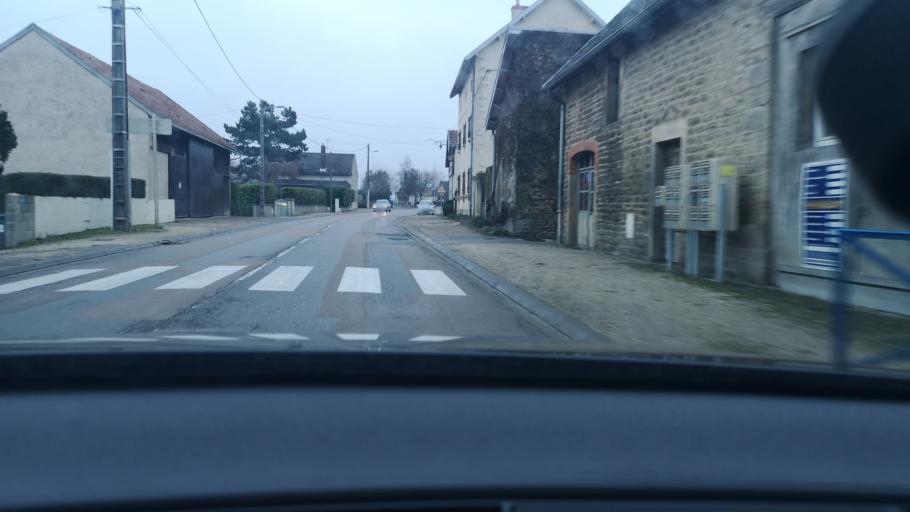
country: FR
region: Bourgogne
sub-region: Departement de la Cote-d'Or
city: Fenay
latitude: 47.2231
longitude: 5.0625
